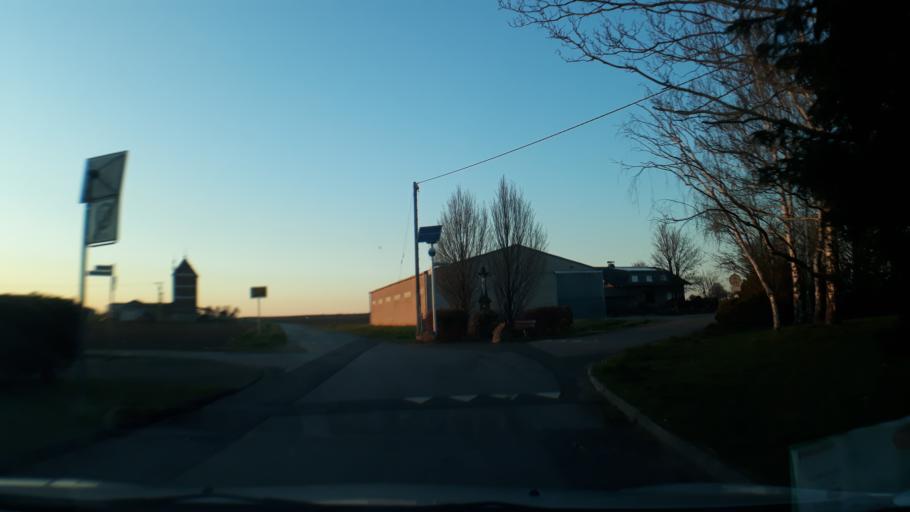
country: DE
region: North Rhine-Westphalia
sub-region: Regierungsbezirk Koln
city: Vettweiss
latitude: 50.7050
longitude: 6.6201
